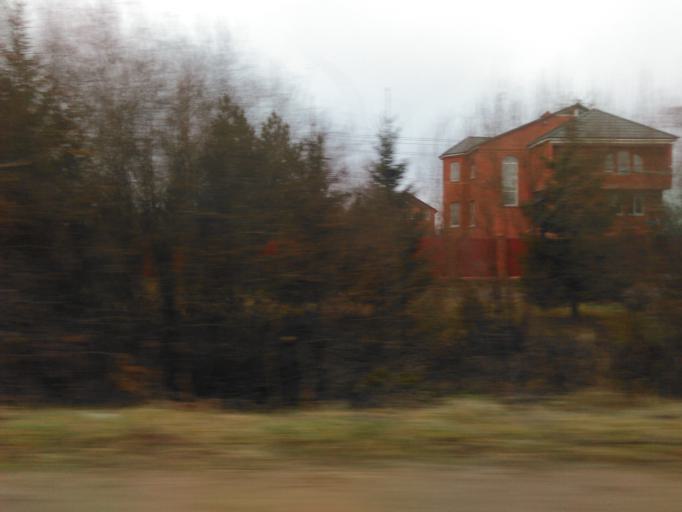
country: RU
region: Moskovskaya
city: Ashukino
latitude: 56.1737
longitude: 37.9392
